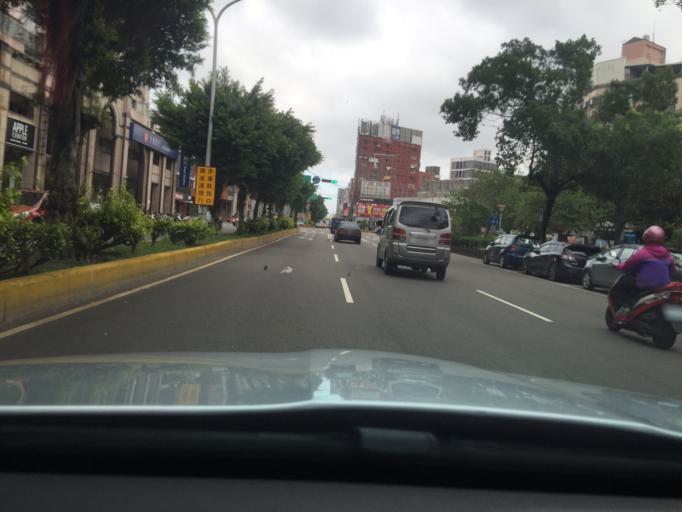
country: TW
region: Taiwan
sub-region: Hsinchu
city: Hsinchu
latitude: 24.8144
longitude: 120.9759
